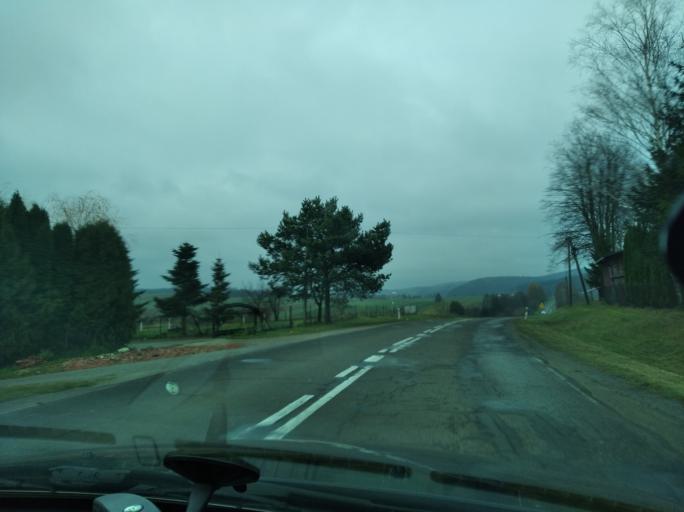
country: PL
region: Subcarpathian Voivodeship
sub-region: Powiat rzeszowski
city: Dynow
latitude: 49.8458
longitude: 22.2437
